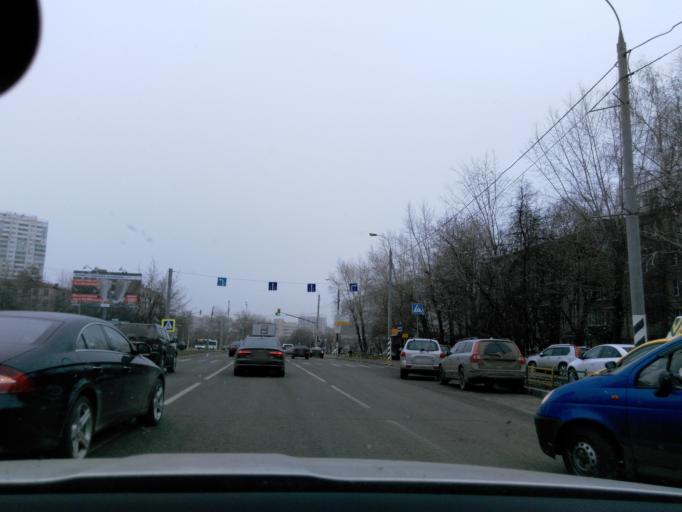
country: RU
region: Moscow
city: Novyye Cheremushki
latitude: 55.6829
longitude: 37.5875
